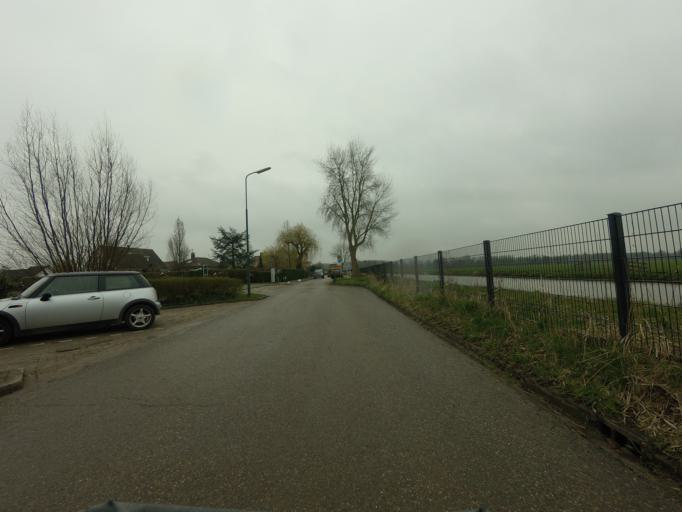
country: NL
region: Utrecht
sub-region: Stichtse Vecht
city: Breukelen
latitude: 52.1818
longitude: 5.0194
